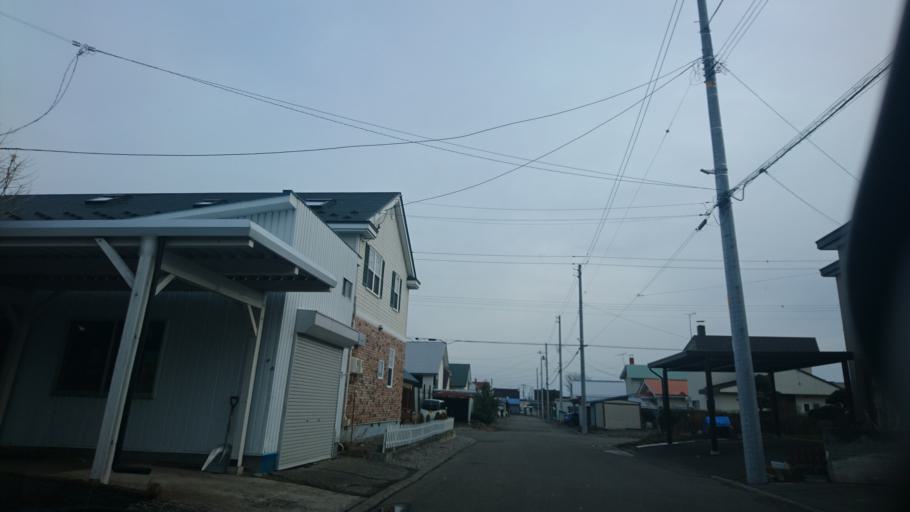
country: JP
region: Hokkaido
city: Otofuke
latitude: 42.9950
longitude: 143.1909
